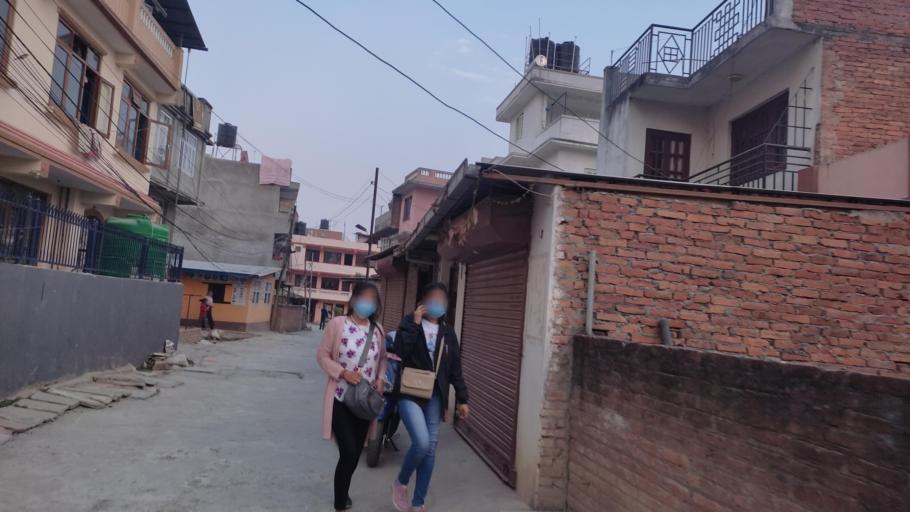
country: NP
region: Central Region
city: Kirtipur
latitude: 27.6699
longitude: 85.2798
